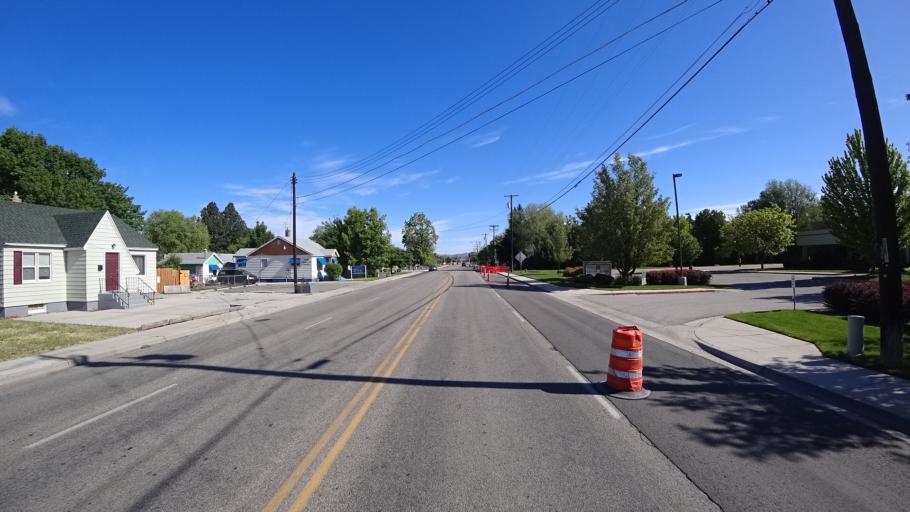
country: US
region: Idaho
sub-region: Ada County
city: Garden City
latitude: 43.5996
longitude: -116.2436
